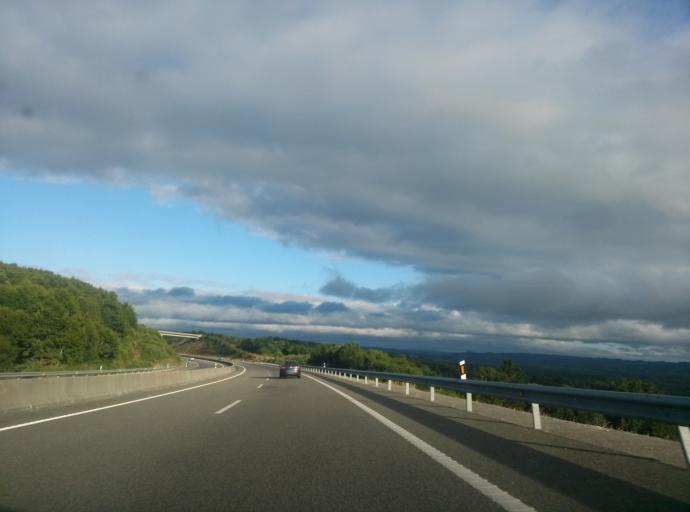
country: ES
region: Galicia
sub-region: Provincia de Lugo
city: Vilalba
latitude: 43.3635
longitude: -7.7748
